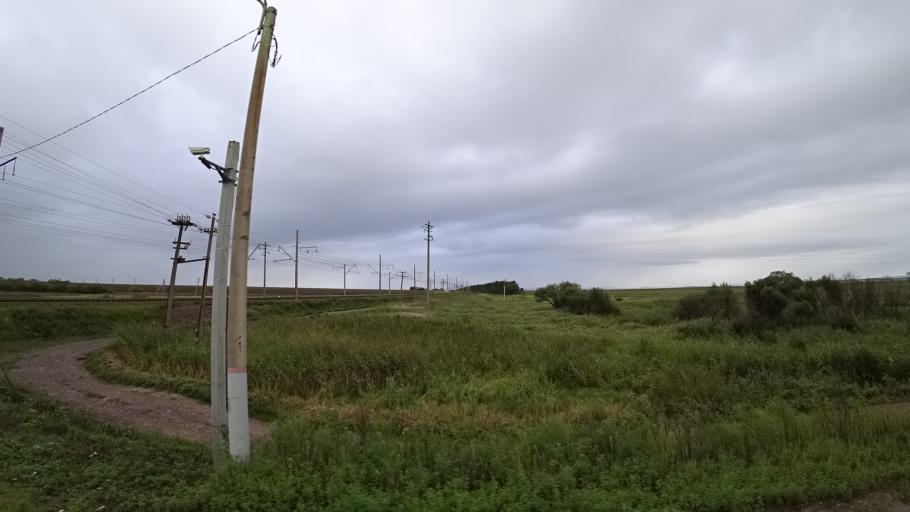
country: RU
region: Primorskiy
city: Chernigovka
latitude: 44.3635
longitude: 132.5512
